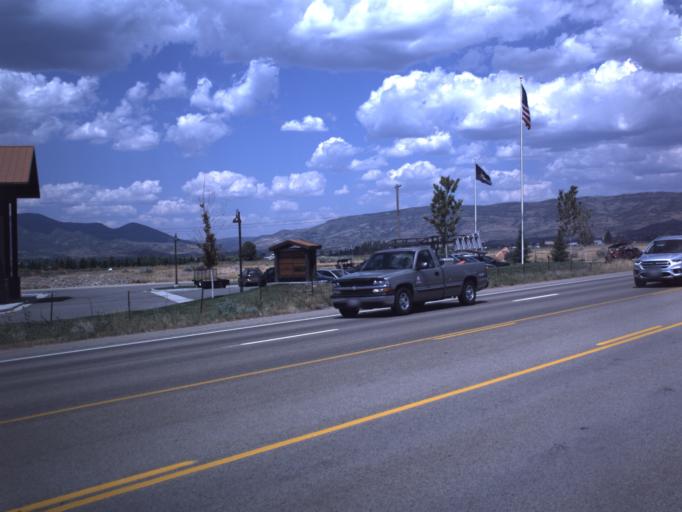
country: US
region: Utah
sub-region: Wasatch County
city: Midway
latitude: 40.4699
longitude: -111.4494
